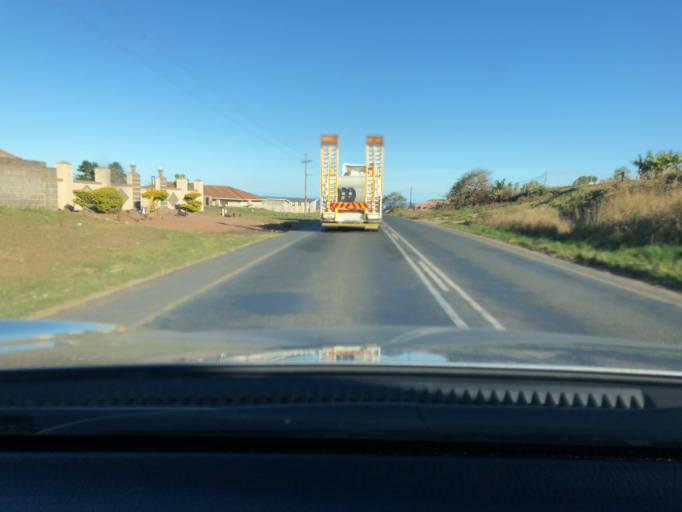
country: ZA
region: KwaZulu-Natal
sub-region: eThekwini Metropolitan Municipality
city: Umkomaas
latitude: -30.0094
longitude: 30.8043
